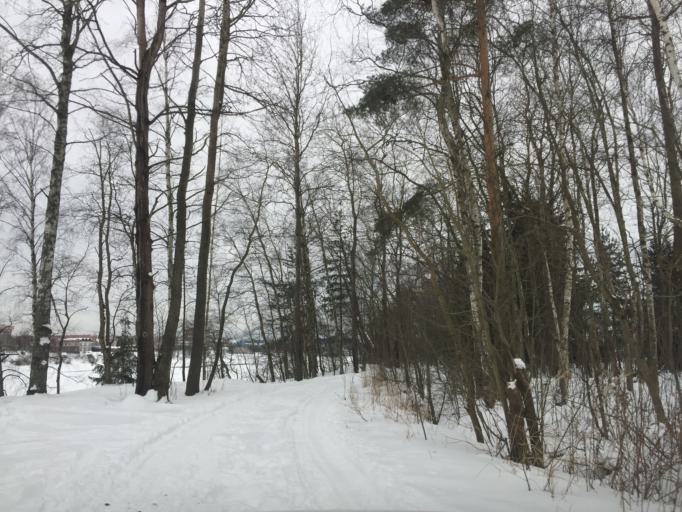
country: RU
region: Leningrad
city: Otradnoye
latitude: 59.7791
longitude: 30.7876
